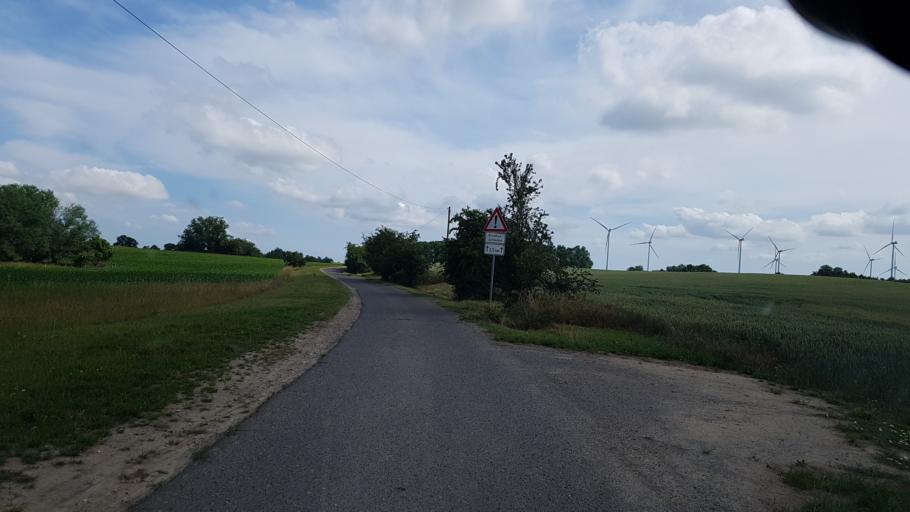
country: DE
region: Brandenburg
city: Prenzlau
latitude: 53.3837
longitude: 13.8087
